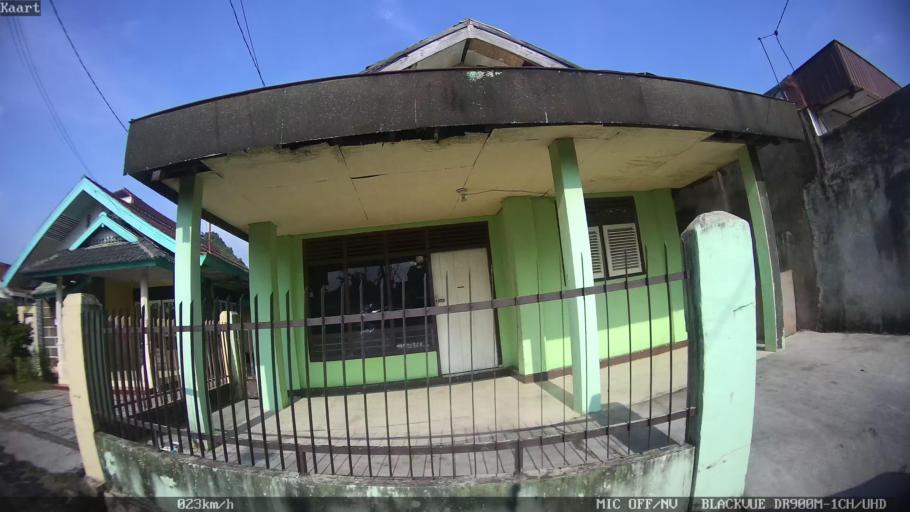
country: ID
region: Lampung
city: Kedaton
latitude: -5.3882
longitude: 105.2634
